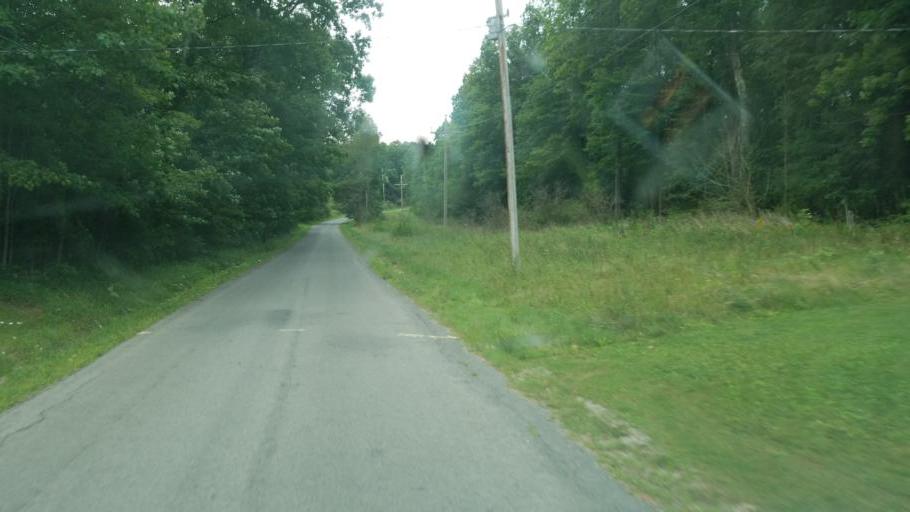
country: US
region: Pennsylvania
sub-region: Clarion County
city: Marianne
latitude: 41.2119
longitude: -79.4267
